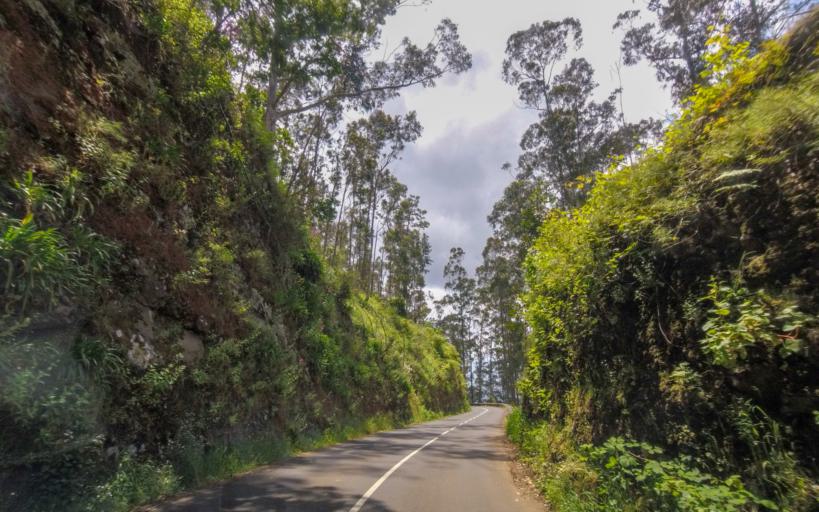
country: PT
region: Madeira
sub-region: Funchal
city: Nossa Senhora do Monte
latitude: 32.6783
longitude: -16.8810
